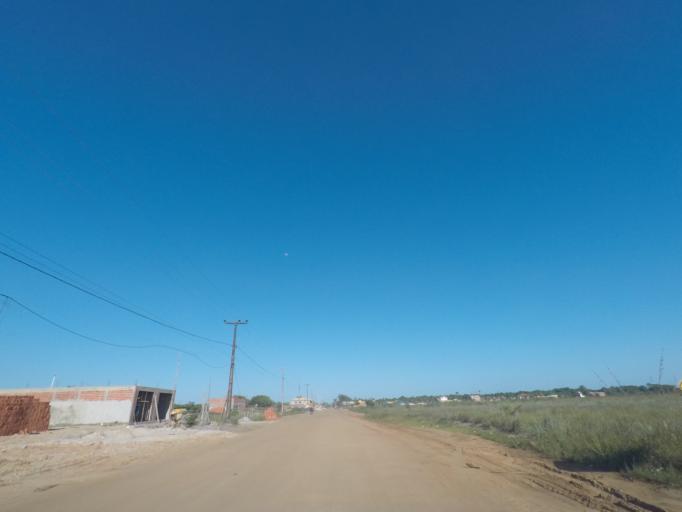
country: BR
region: Bahia
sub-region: Camamu
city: Camamu
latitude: -13.9323
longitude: -38.9426
